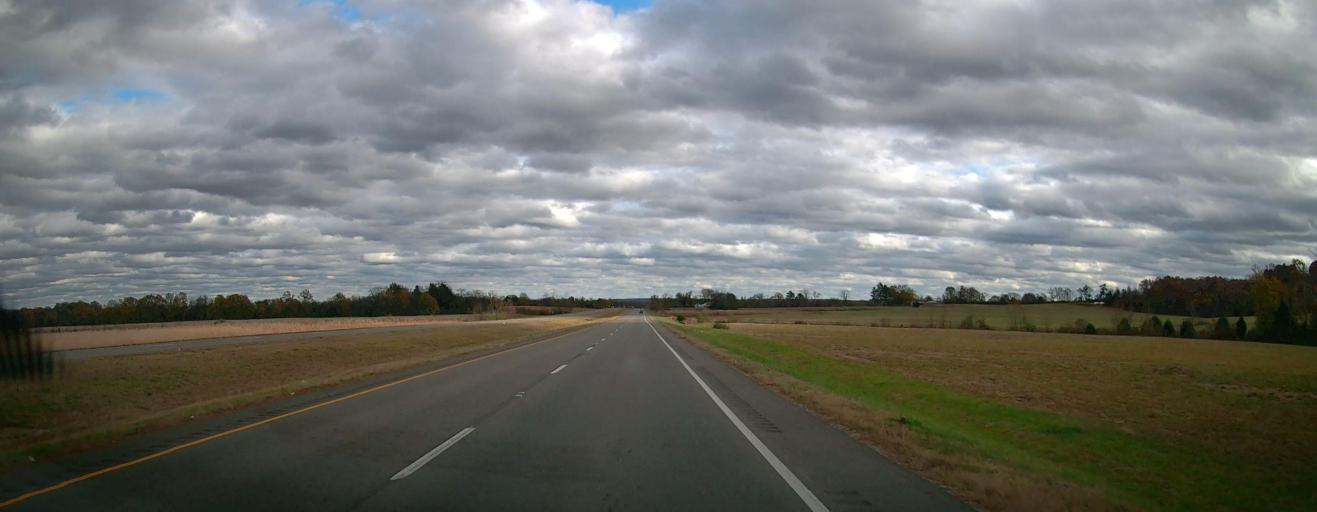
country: US
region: Alabama
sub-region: Morgan County
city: Danville
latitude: 34.3845
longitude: -87.1027
